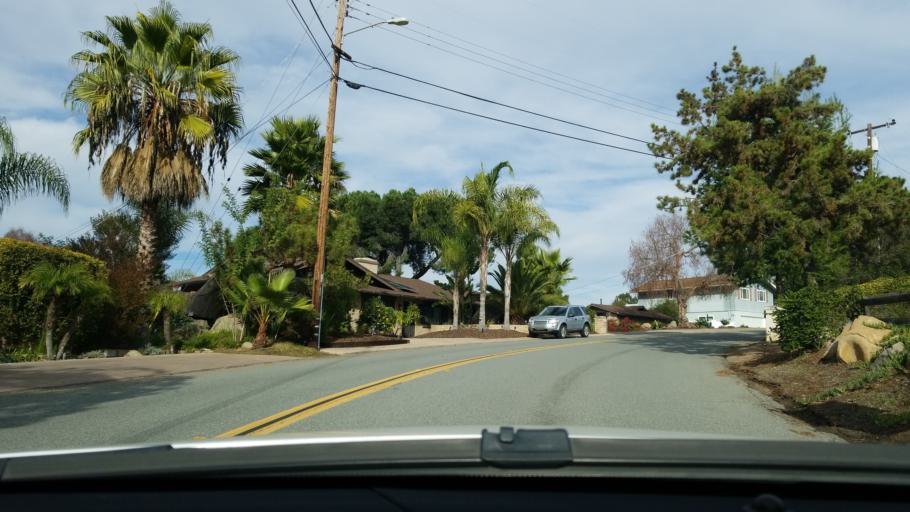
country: US
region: California
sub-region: San Diego County
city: Casa de Oro-Mount Helix
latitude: 32.7682
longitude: -116.9569
